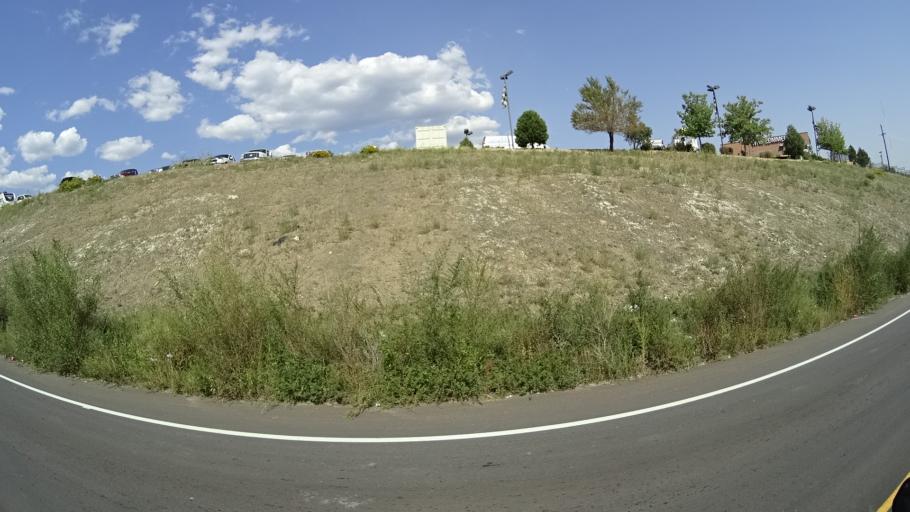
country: US
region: Colorado
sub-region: El Paso County
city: Colorado Springs
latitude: 38.8233
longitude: -104.8420
